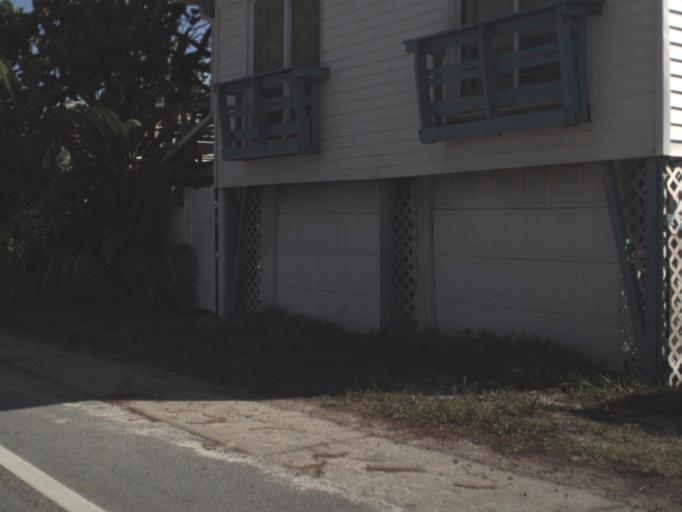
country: US
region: Florida
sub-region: Manatee County
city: Bradenton Beach
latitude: 27.4590
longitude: -82.6964
